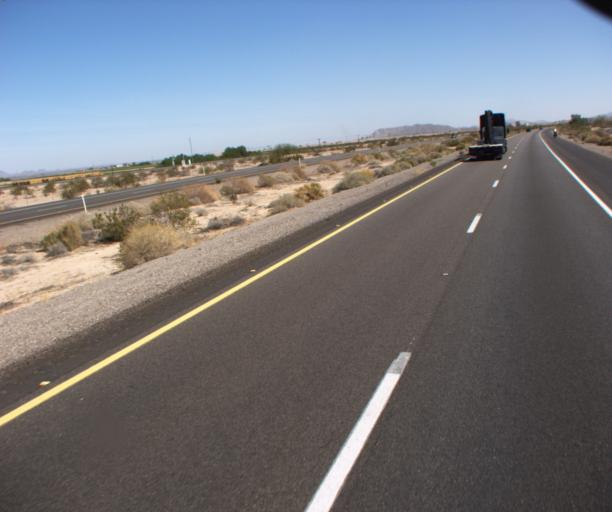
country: US
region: Arizona
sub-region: Yuma County
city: Wellton
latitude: 32.6710
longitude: -114.1027
